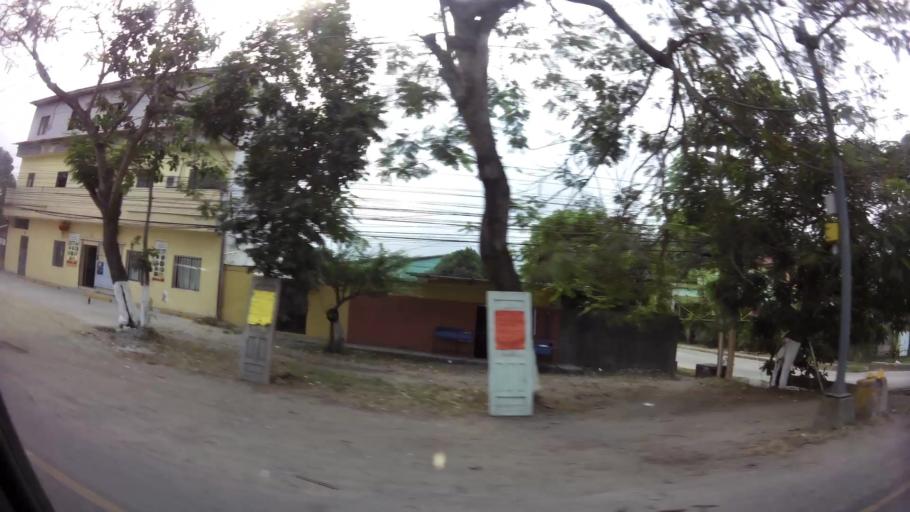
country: HN
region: Yoro
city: El Progreso
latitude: 15.4106
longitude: -87.8041
